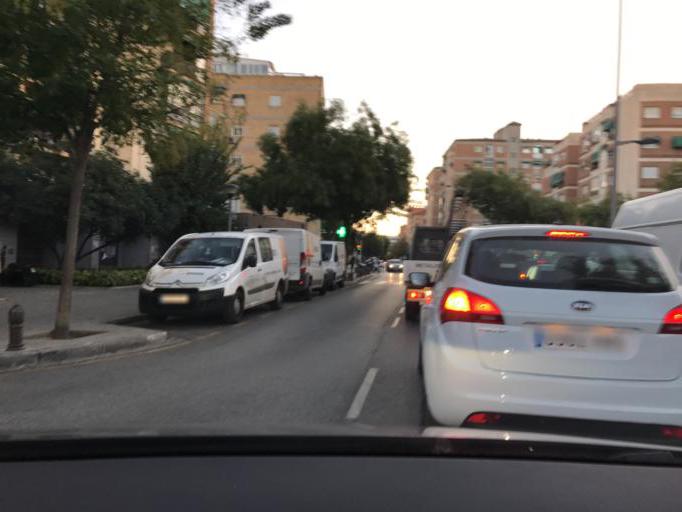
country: ES
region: Andalusia
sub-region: Provincia de Granada
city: Armilla
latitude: 37.1571
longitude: -3.6026
